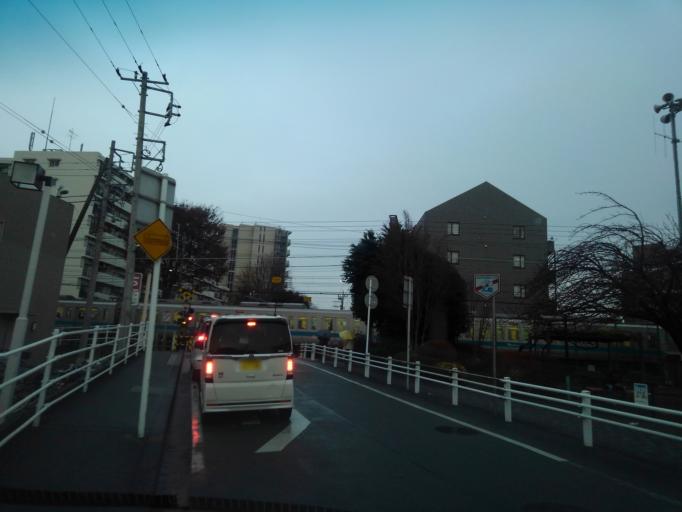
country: JP
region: Tokyo
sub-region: Machida-shi
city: Machida
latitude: 35.5183
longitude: 139.4397
